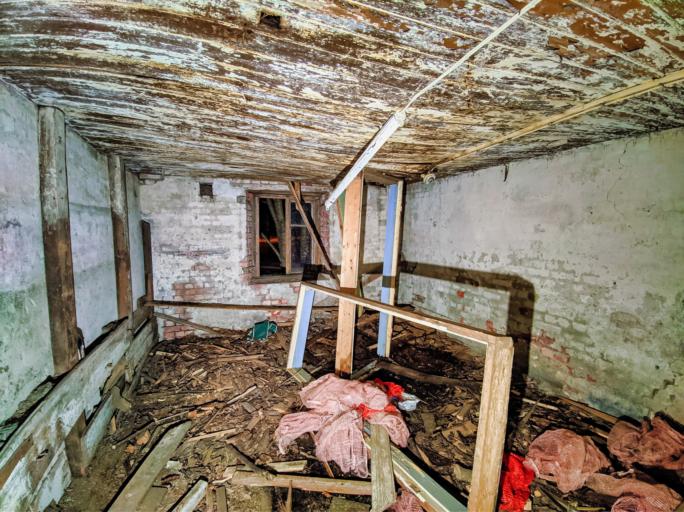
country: NO
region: Aust-Agder
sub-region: Arendal
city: Arendal
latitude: 58.4347
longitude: 8.7431
